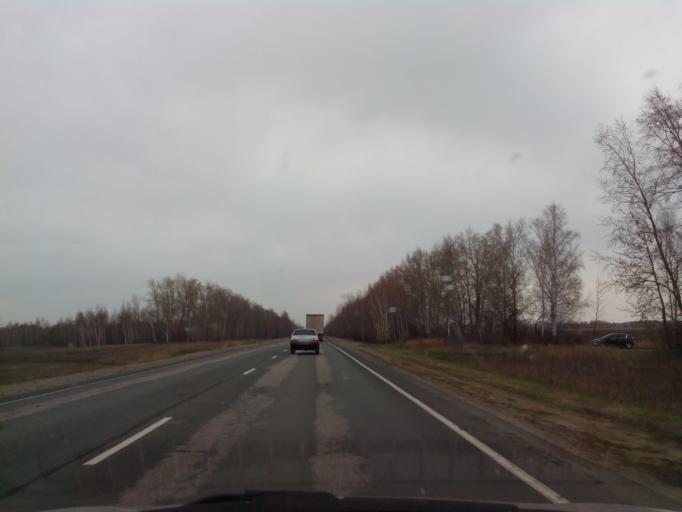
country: RU
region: Tambov
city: Pervomayskiy
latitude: 53.1023
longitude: 40.3945
